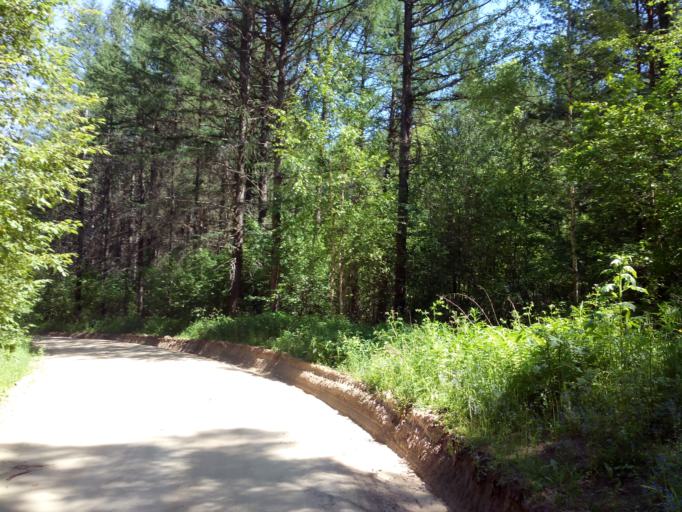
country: RU
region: Moskovskaya
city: Bogorodskoye
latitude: 56.5164
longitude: 38.1945
